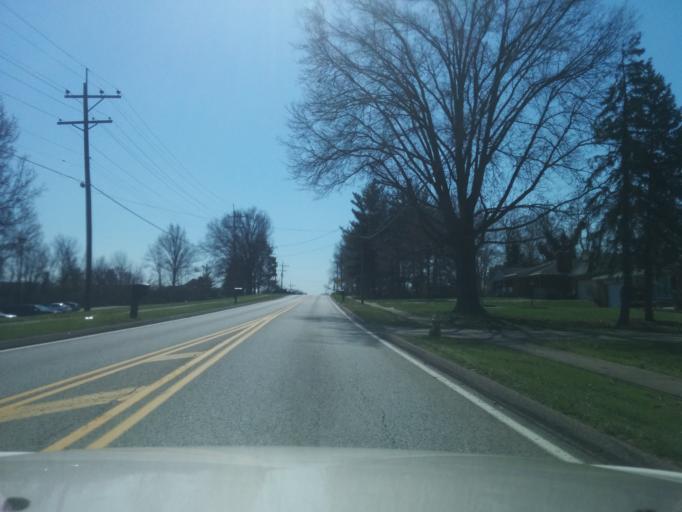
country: US
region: Ohio
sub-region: Hamilton County
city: Groesbeck
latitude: 39.2343
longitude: -84.5990
